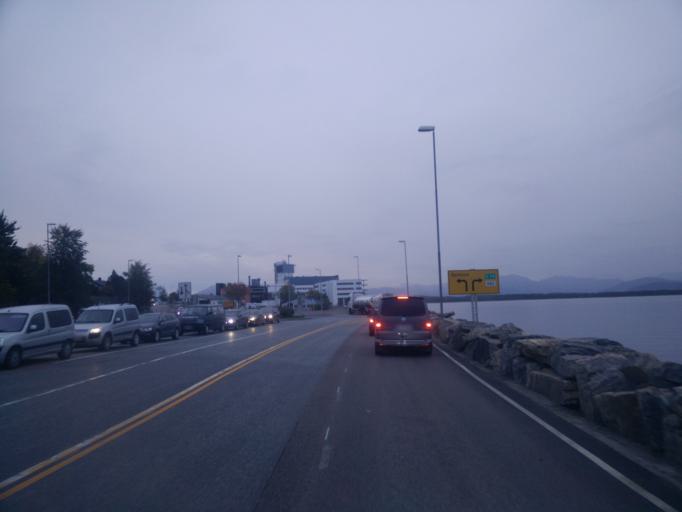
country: NO
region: More og Romsdal
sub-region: Molde
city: Molde
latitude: 62.7368
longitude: 7.1732
